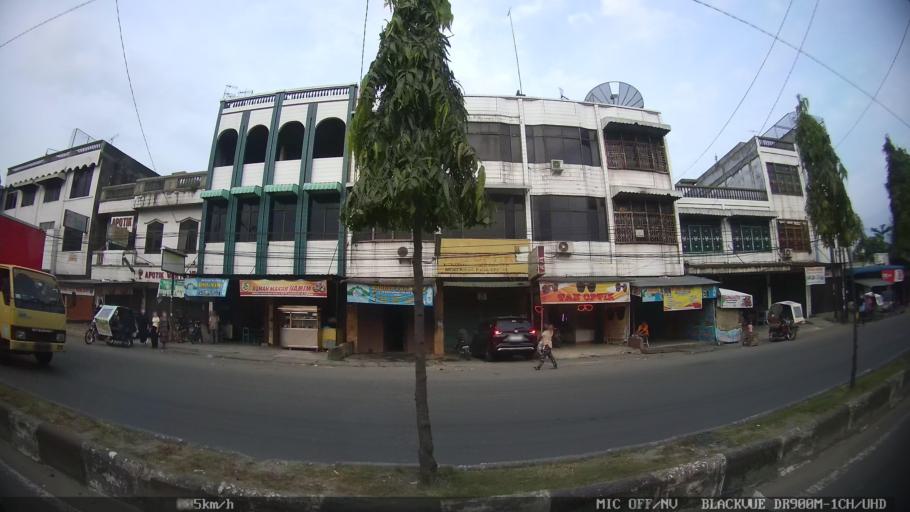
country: ID
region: North Sumatra
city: Sunggal
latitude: 3.5971
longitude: 98.6090
